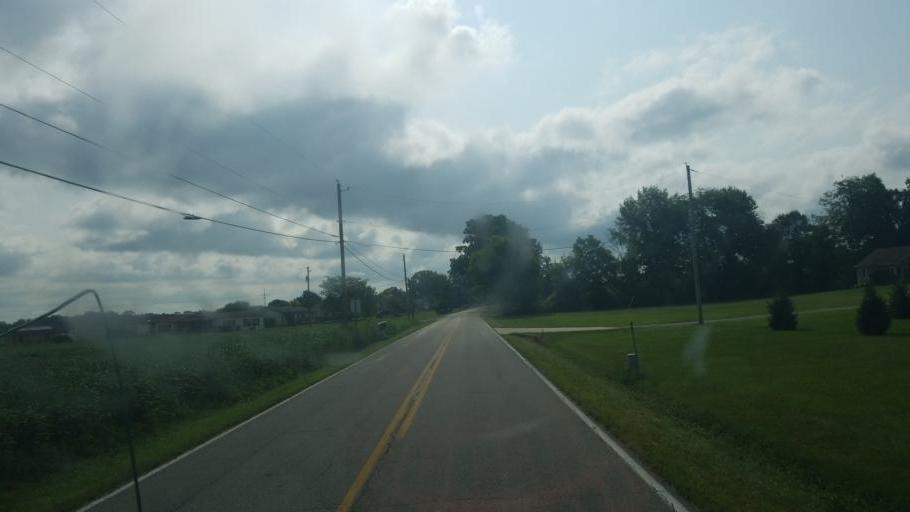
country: US
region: Ohio
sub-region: Marion County
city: Marion
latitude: 40.5637
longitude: -83.0065
